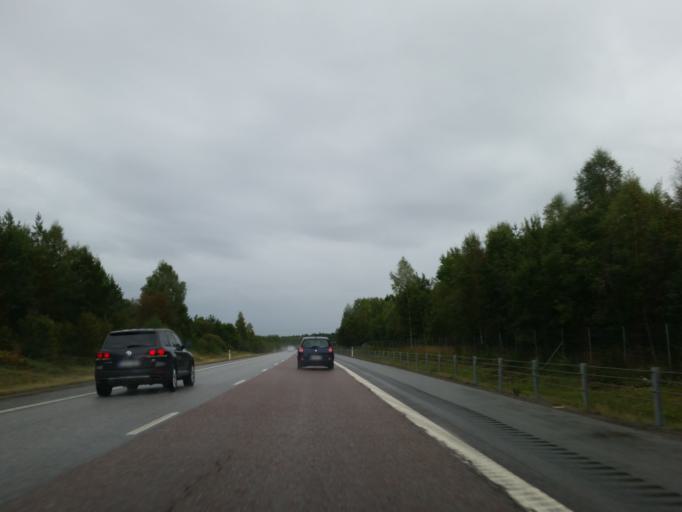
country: SE
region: Uppsala
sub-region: Enkopings Kommun
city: Dalby
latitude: 59.6087
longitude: 17.4202
